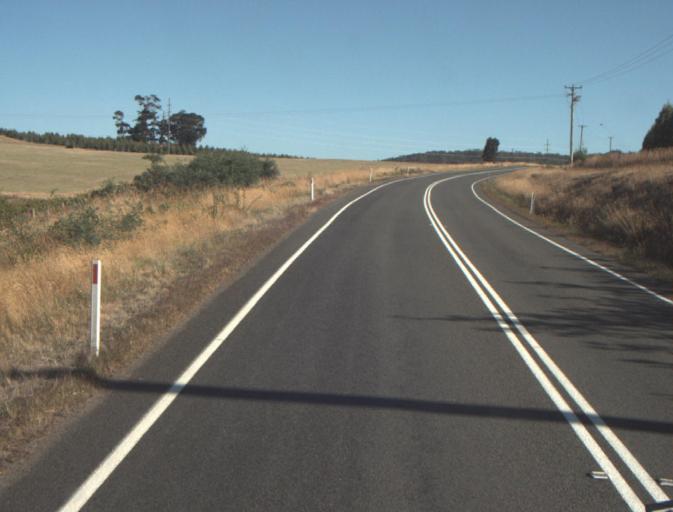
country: AU
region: Tasmania
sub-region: Launceston
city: Newstead
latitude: -41.4151
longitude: 147.2806
